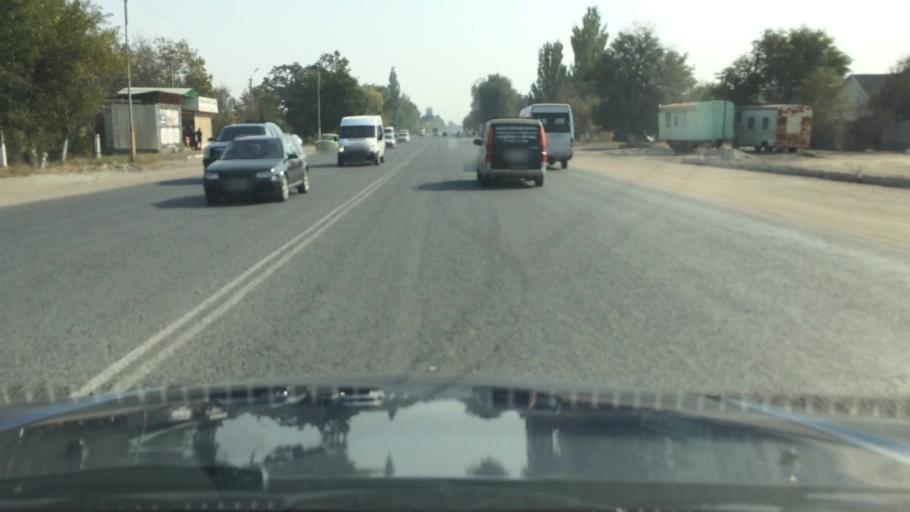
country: KG
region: Chuy
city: Lebedinovka
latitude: 42.8873
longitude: 74.6694
